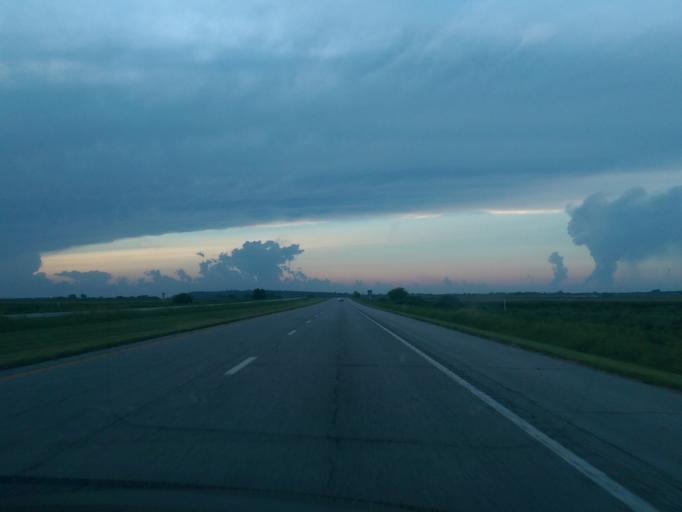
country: US
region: Iowa
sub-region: Fremont County
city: Hamburg
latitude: 40.5073
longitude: -95.6008
